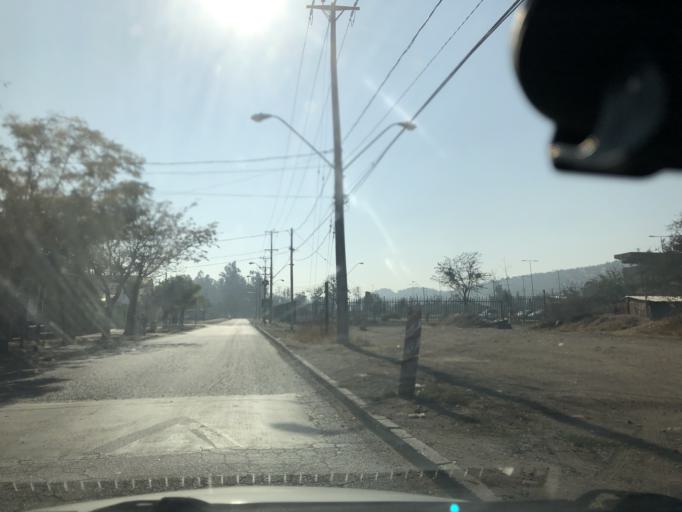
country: CL
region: Santiago Metropolitan
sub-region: Provincia de Cordillera
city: Puente Alto
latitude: -33.6121
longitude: -70.5492
